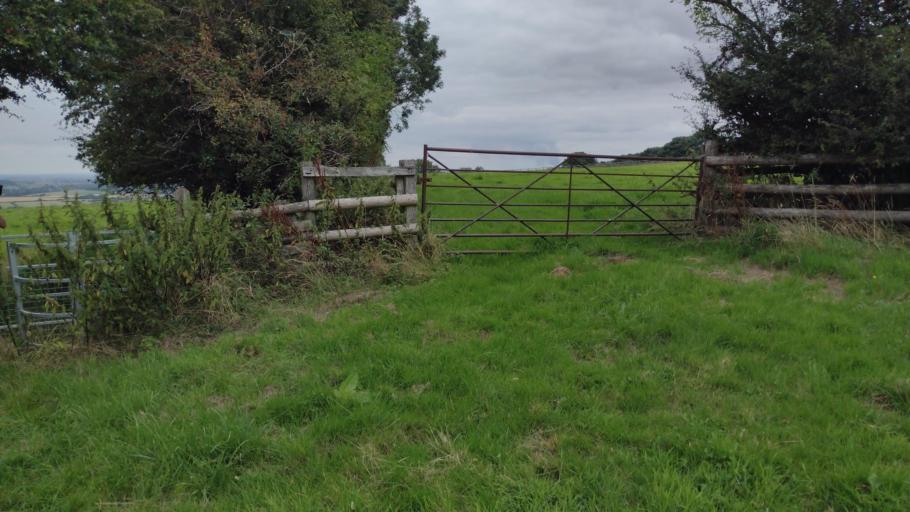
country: GB
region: England
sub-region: Warwickshire
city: Shipston on Stour
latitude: 52.0387
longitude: -1.5819
